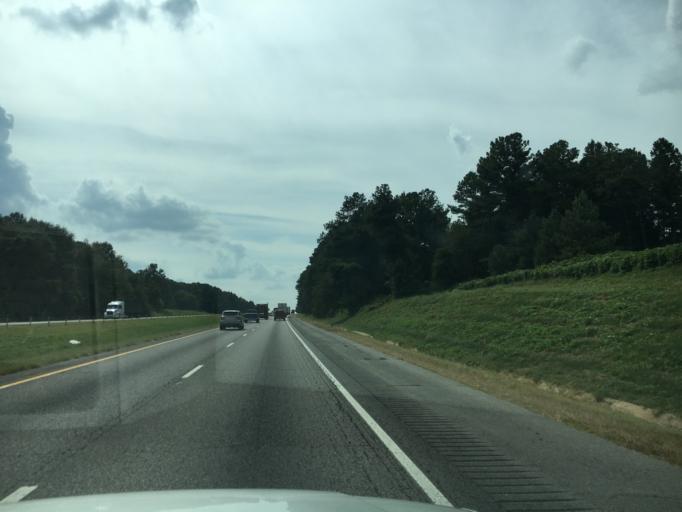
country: US
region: Georgia
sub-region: Jackson County
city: Braselton
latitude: 34.1290
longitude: -83.7065
